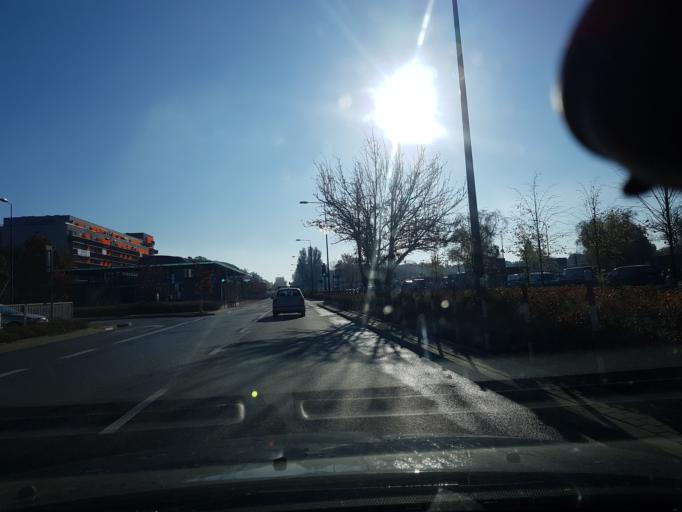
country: PL
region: Masovian Voivodeship
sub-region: Warszawa
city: Bielany
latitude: 52.2871
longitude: 20.9373
